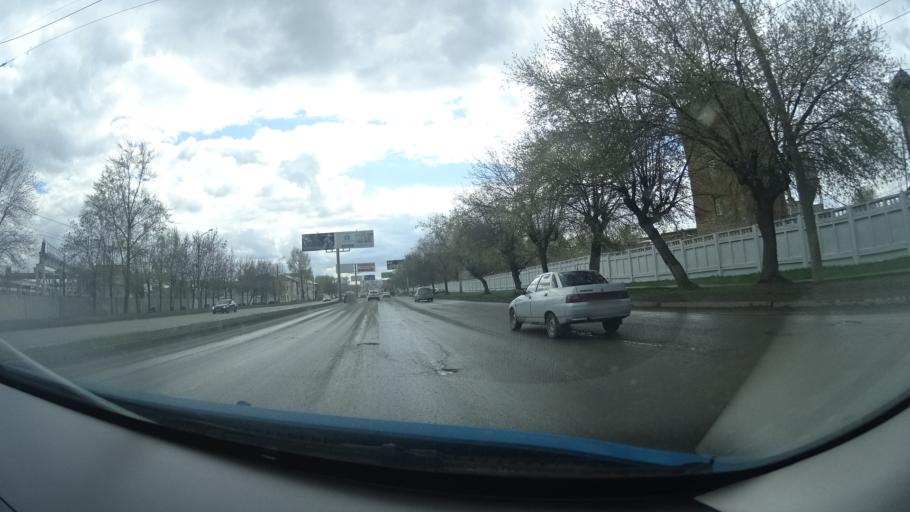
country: RU
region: Bashkortostan
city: Ufa
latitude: 54.8034
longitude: 56.0813
